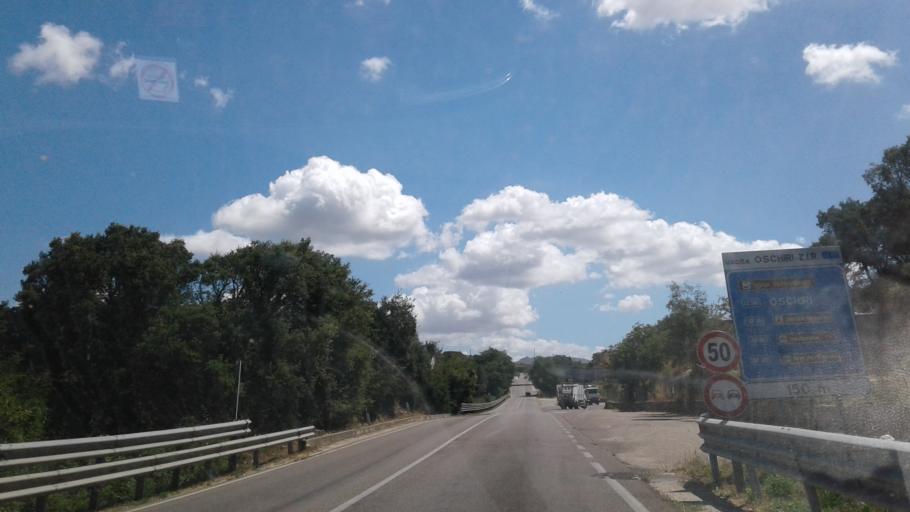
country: IT
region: Sardinia
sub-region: Provincia di Olbia-Tempio
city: Tempio Pausania
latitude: 40.9064
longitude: 9.1419
